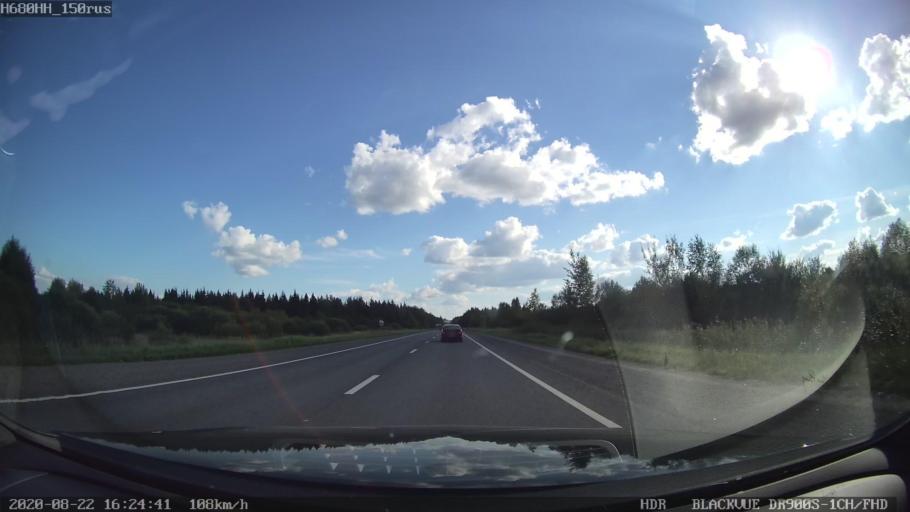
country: RU
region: Tverskaya
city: Rameshki
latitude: 57.3330
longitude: 36.0938
